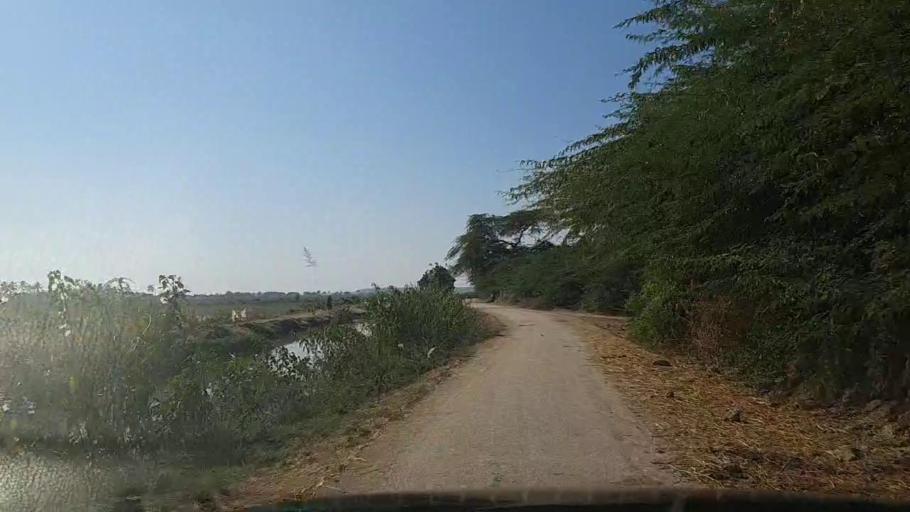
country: PK
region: Sindh
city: Thatta
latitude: 24.6366
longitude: 67.8751
